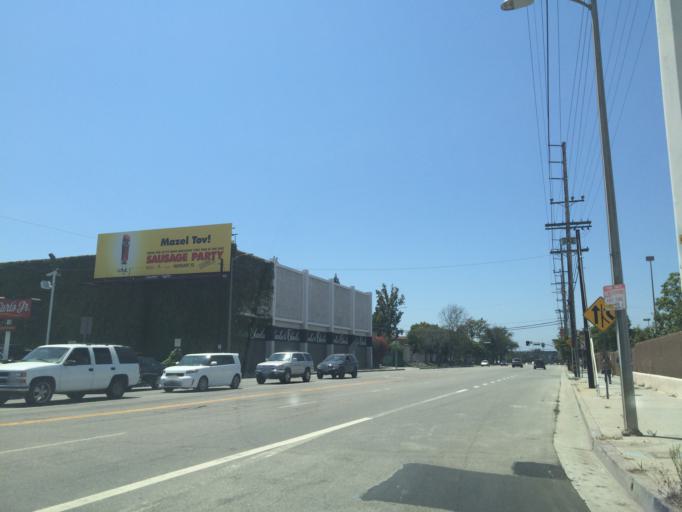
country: US
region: California
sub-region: Los Angeles County
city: Culver City
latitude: 34.0218
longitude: -118.3726
